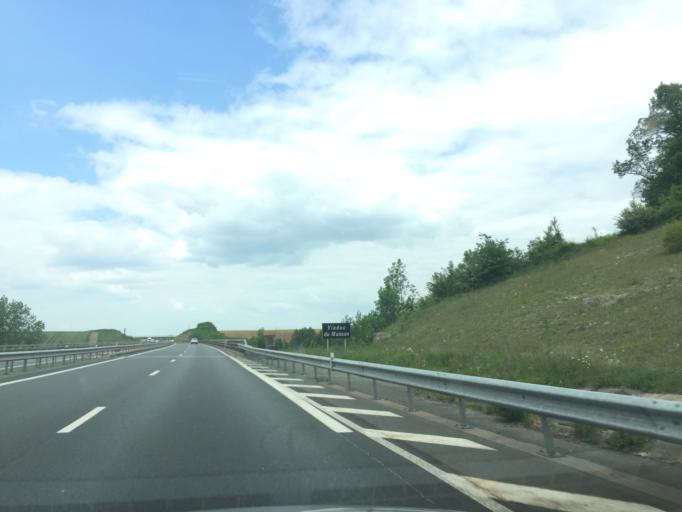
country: FR
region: Poitou-Charentes
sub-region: Departement des Deux-Sevres
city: Chauray
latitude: 46.3816
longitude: -0.3642
